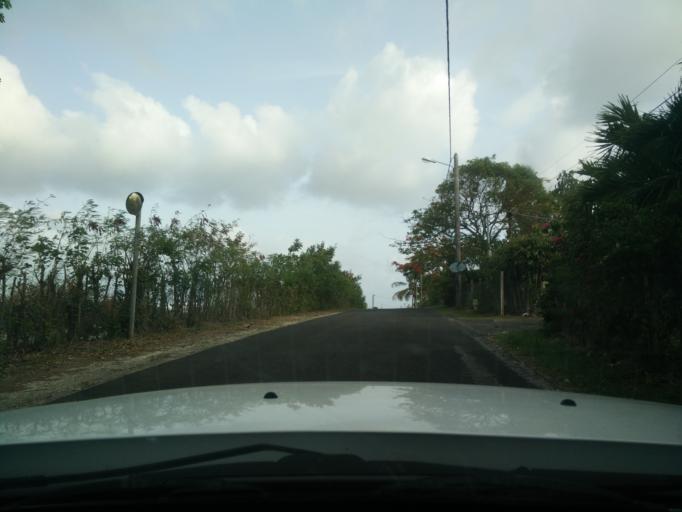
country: GP
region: Guadeloupe
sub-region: Guadeloupe
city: Sainte-Anne
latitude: 16.2511
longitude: -61.3319
